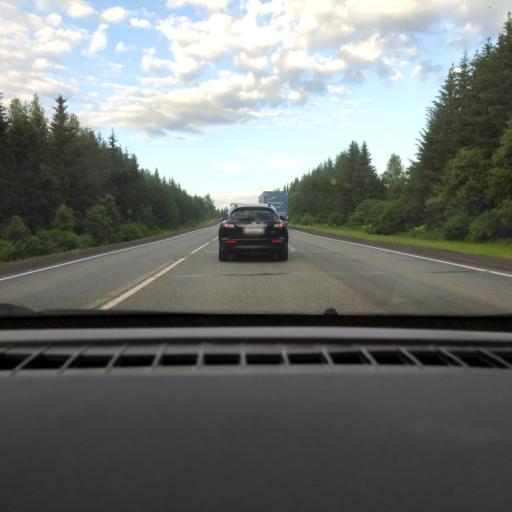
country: RU
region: Perm
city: Nytva
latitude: 57.9340
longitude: 55.1144
